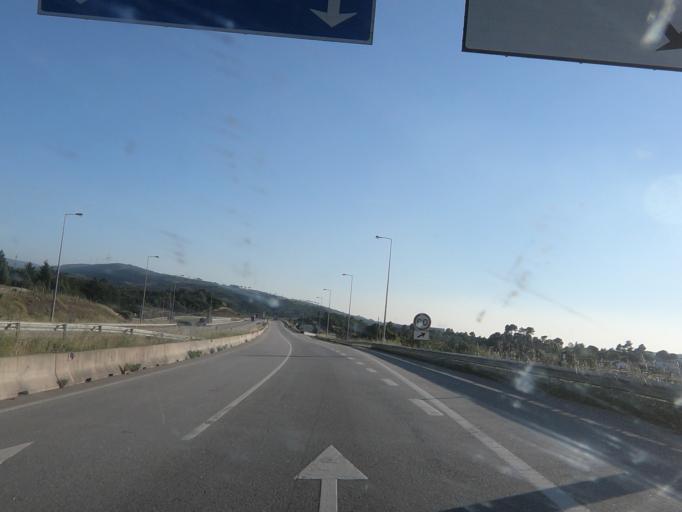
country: PT
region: Guarda
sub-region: Celorico da Beira
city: Celorico da Beira
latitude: 40.6383
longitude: -7.3478
